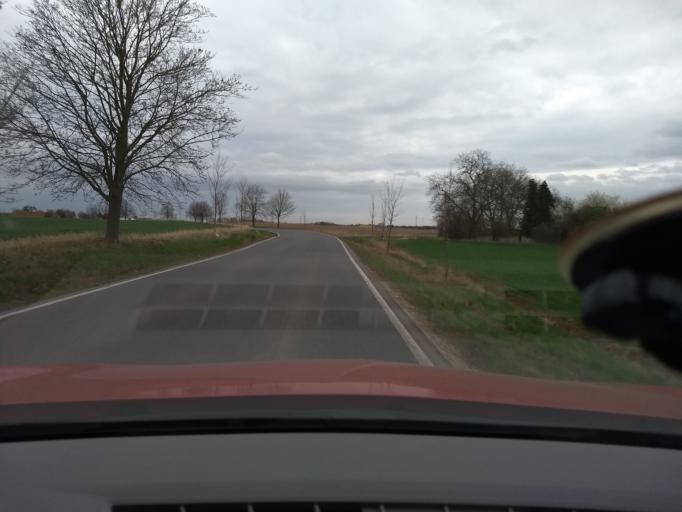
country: CZ
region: Central Bohemia
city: Unhost'
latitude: 50.0559
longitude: 14.1674
